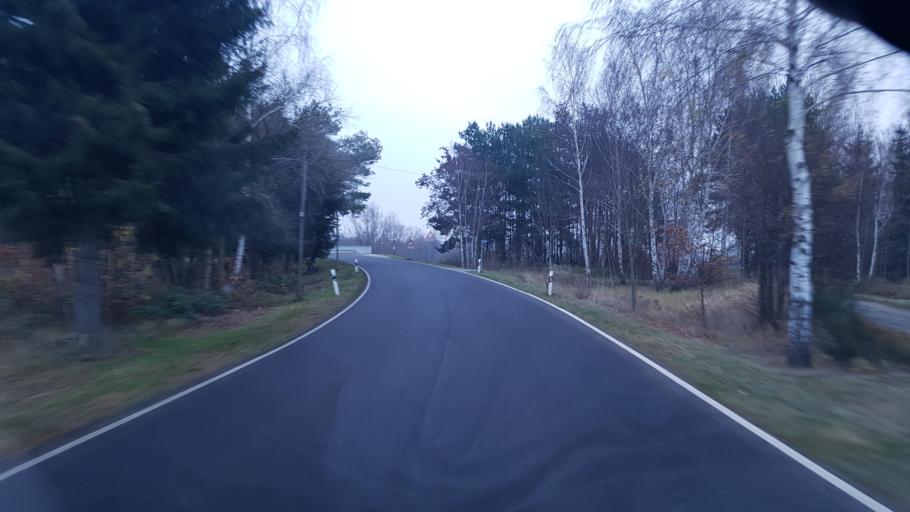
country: DE
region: Brandenburg
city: Werben
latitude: 51.8474
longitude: 14.1976
